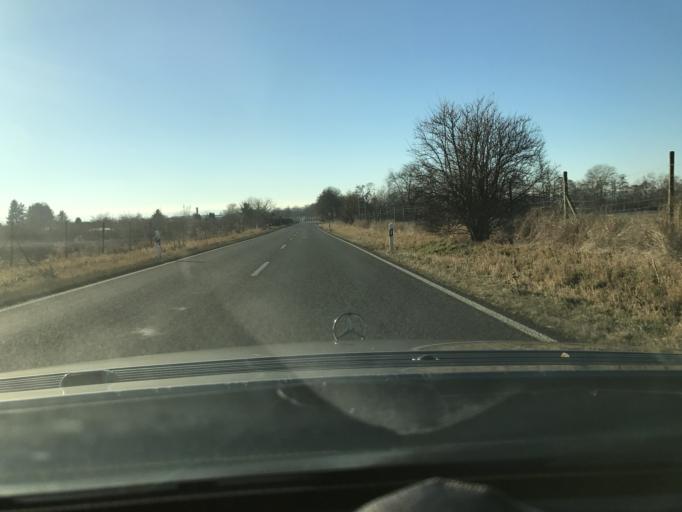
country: DE
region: Thuringia
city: Muehlhausen
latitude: 51.2327
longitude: 10.4811
